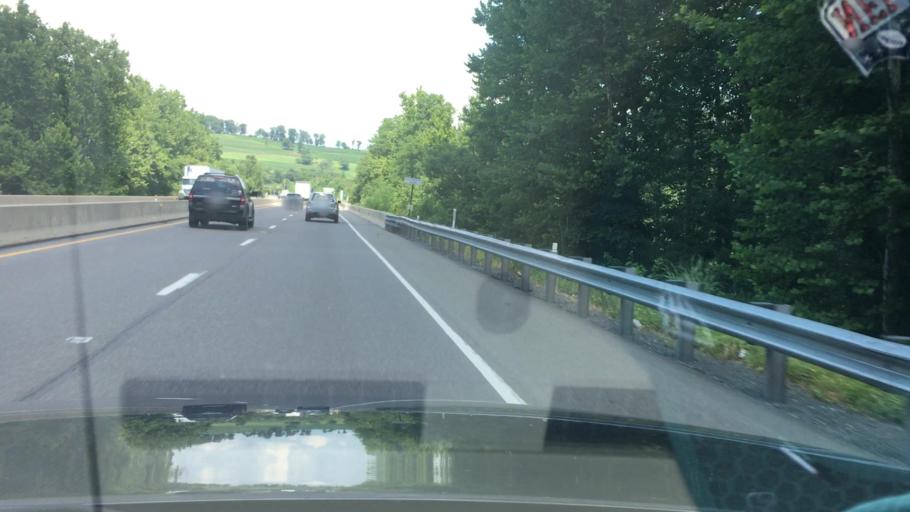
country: US
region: Pennsylvania
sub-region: Berks County
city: West Hamburg
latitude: 40.6054
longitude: -76.0295
